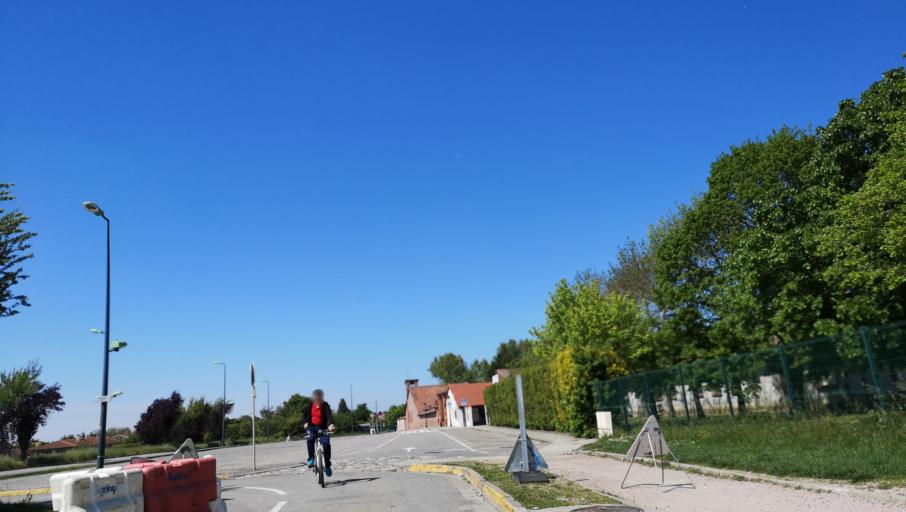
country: FR
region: Midi-Pyrenees
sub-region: Departement de la Haute-Garonne
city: Beauzelle
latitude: 43.6787
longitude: 1.3674
